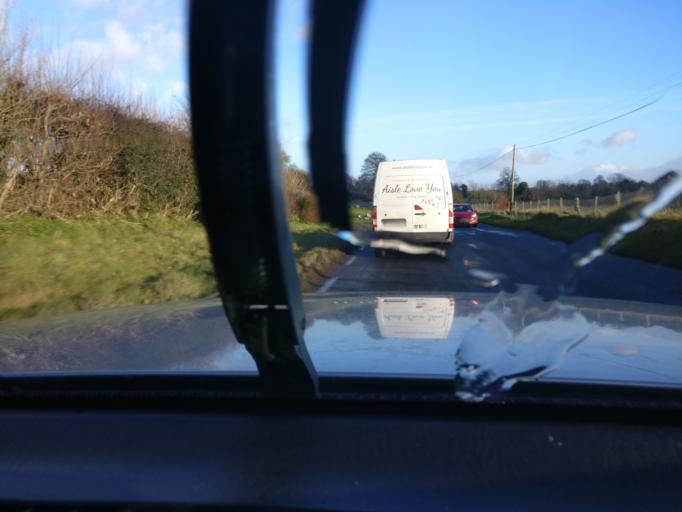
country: IE
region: Leinster
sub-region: An Mhi
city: Kells
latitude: 53.7211
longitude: -6.9637
